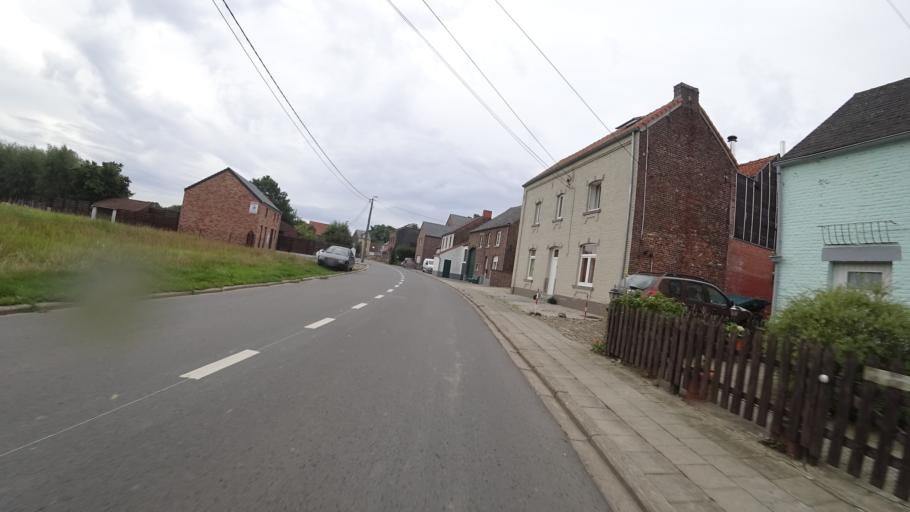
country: BE
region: Wallonia
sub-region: Province du Brabant Wallon
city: Walhain-Saint-Paul
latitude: 50.6137
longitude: 4.7196
